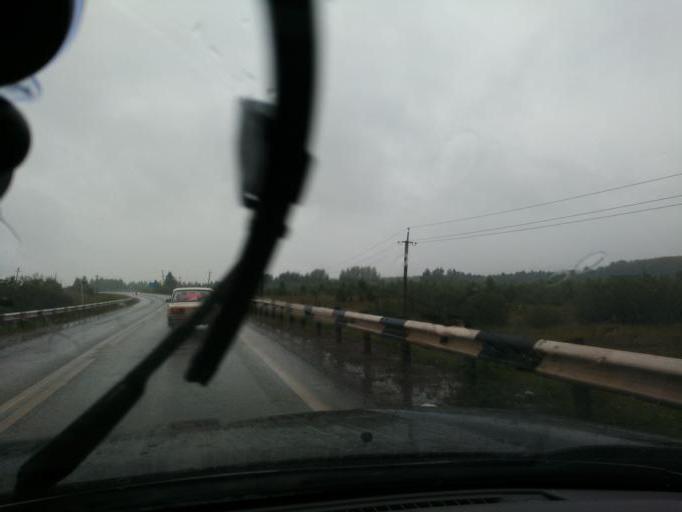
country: RU
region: Perm
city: Osa
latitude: 57.1729
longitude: 55.5322
